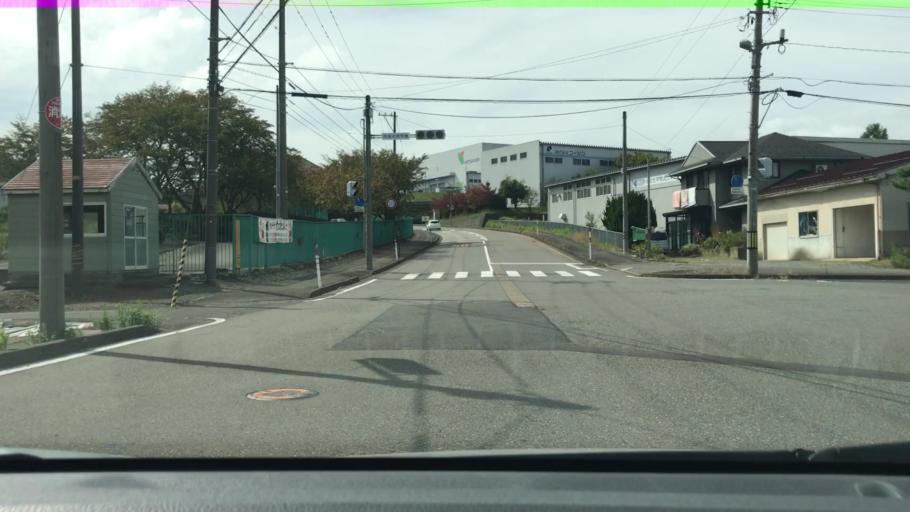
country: JP
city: Asahi
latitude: 36.0138
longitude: 136.1714
